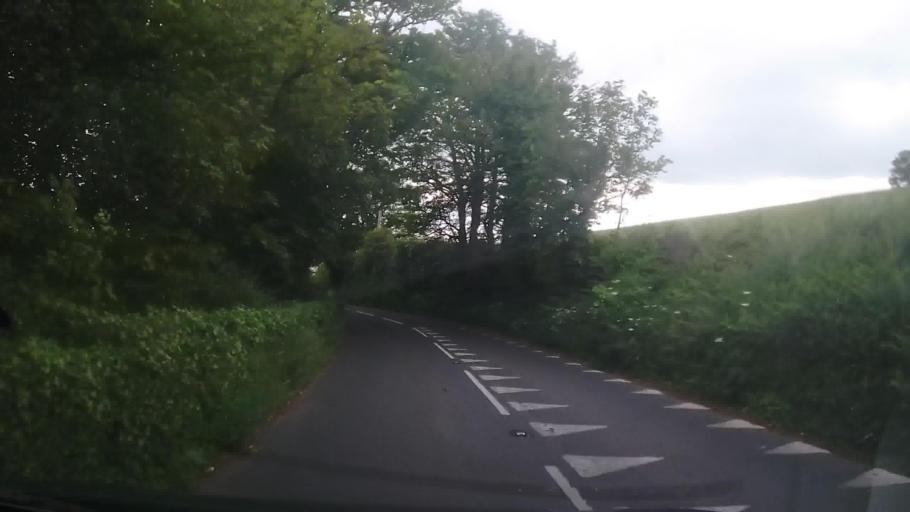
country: GB
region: England
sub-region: Devon
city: Dartmouth
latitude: 50.3055
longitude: -3.6333
